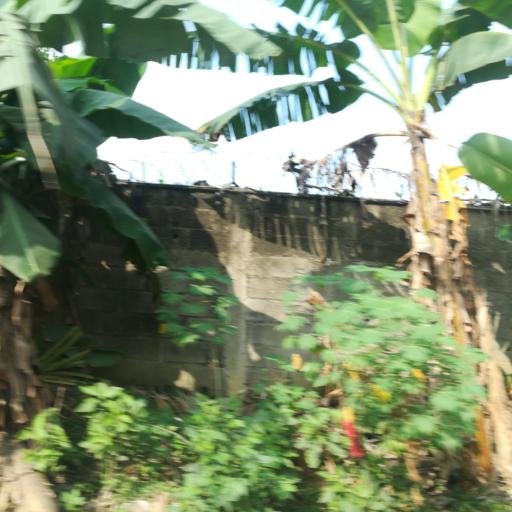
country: NG
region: Rivers
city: Okrika
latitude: 4.7826
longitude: 7.1380
